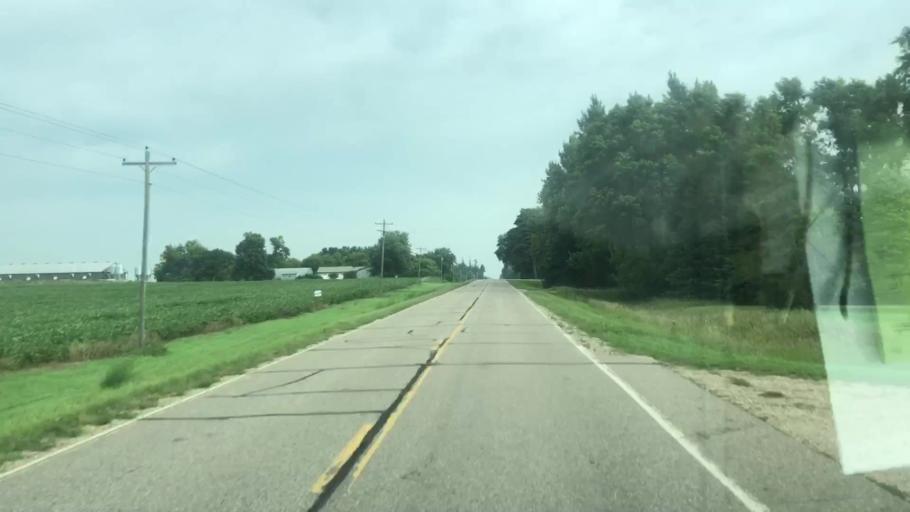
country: US
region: Iowa
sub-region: O'Brien County
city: Sheldon
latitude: 43.2014
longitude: -95.8622
